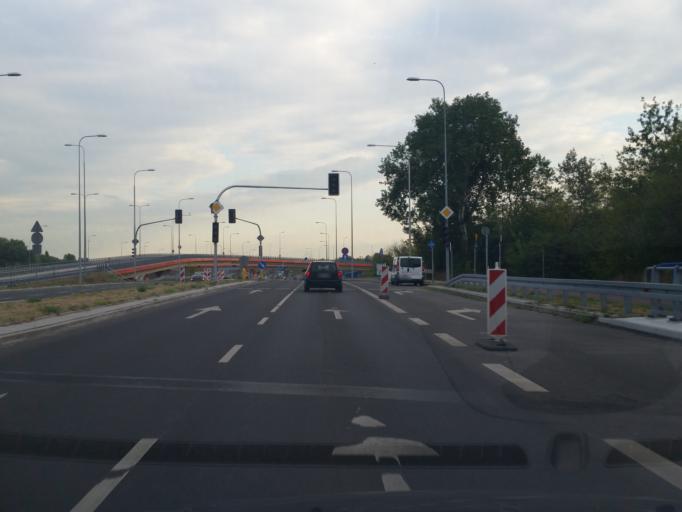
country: PL
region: Masovian Voivodeship
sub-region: Warszawa
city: Wlochy
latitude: 52.1711
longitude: 20.9853
